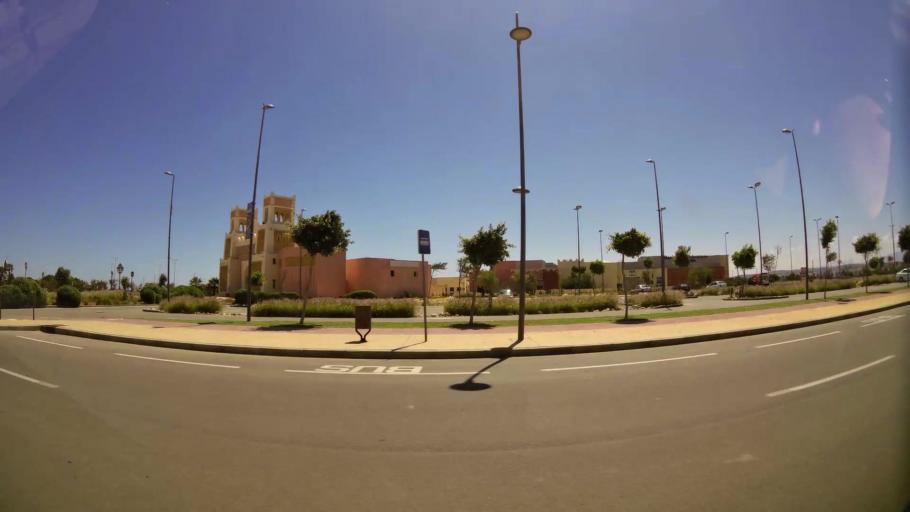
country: MA
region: Oriental
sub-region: Berkane-Taourirt
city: Madagh
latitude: 35.1082
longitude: -2.2996
